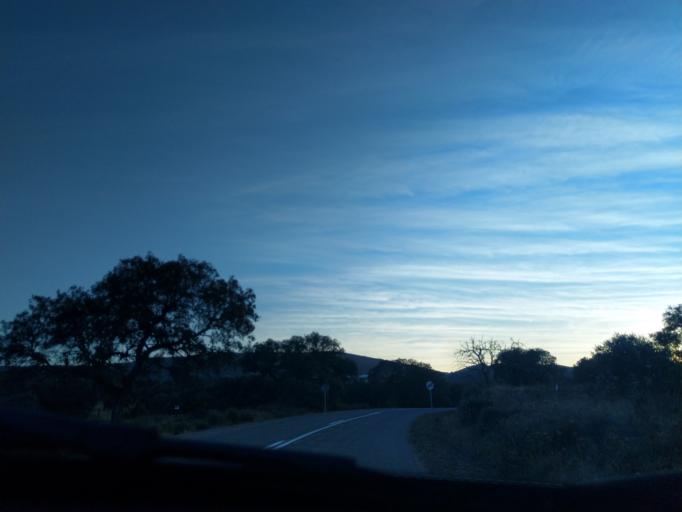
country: ES
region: Extremadura
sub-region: Provincia de Badajoz
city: Reina
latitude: 38.1710
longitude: -5.8761
